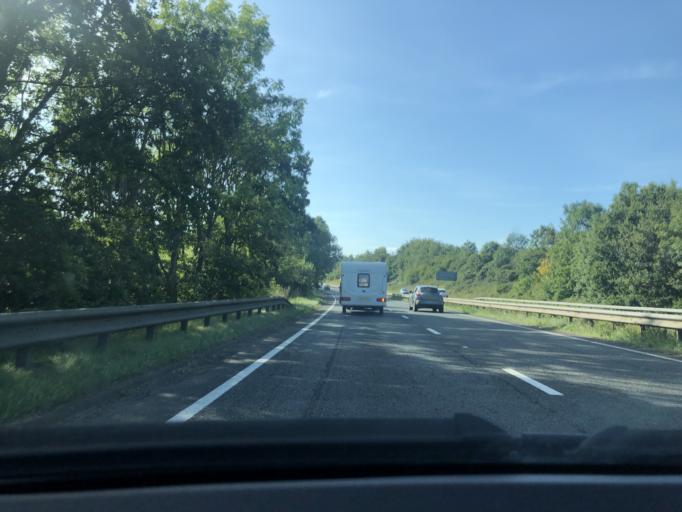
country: GB
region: England
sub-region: Devon
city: Crediton
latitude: 50.7294
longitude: -3.7338
